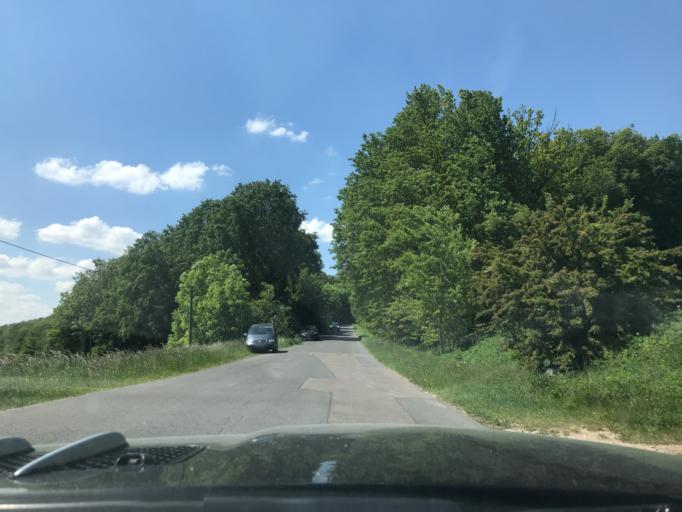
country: DE
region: Thuringia
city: Neuhaus
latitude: 50.7406
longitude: 10.9486
